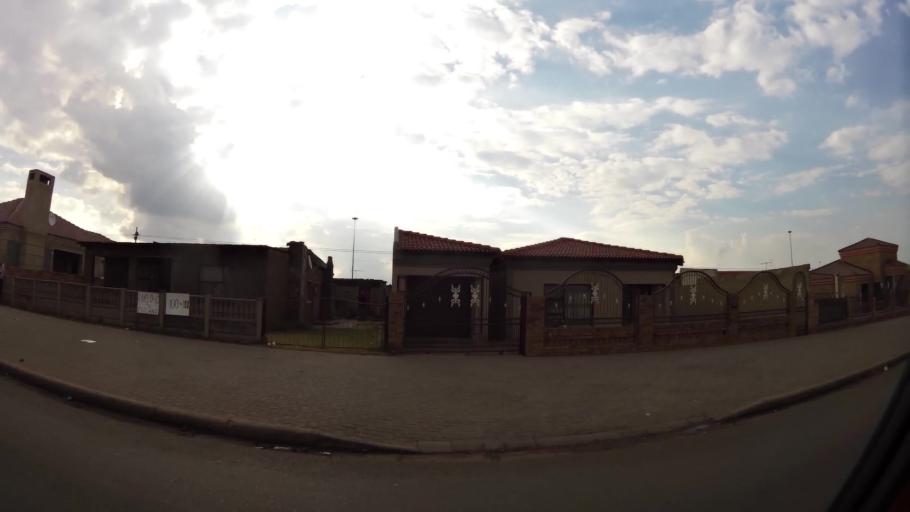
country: ZA
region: Gauteng
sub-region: Sedibeng District Municipality
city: Vanderbijlpark
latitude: -26.6855
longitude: 27.8728
